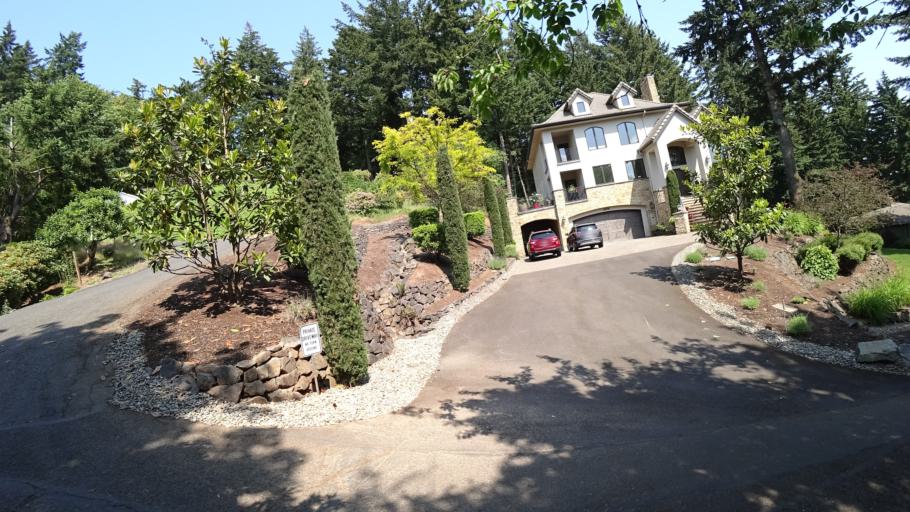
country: US
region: Oregon
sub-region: Clackamas County
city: Happy Valley
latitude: 45.4444
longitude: -122.5544
